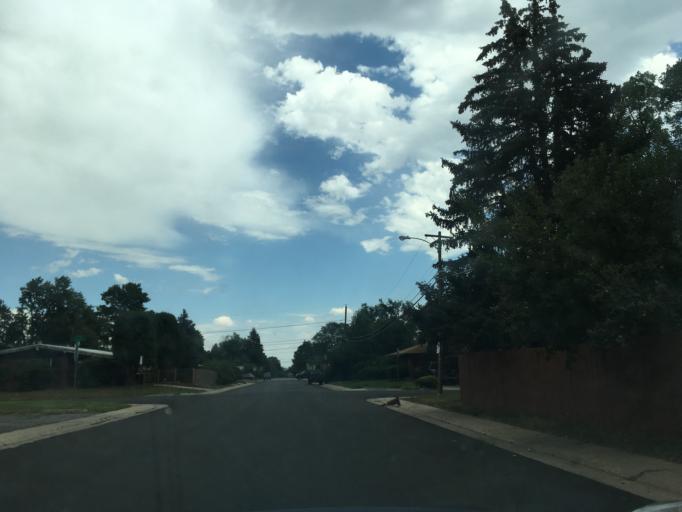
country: US
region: Colorado
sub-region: Arapahoe County
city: Sheridan
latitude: 39.6750
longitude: -105.0432
